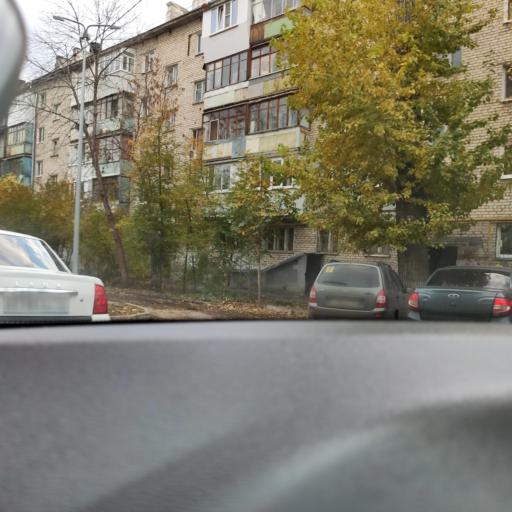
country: RU
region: Samara
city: Petra-Dubrava
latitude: 53.2311
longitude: 50.2761
